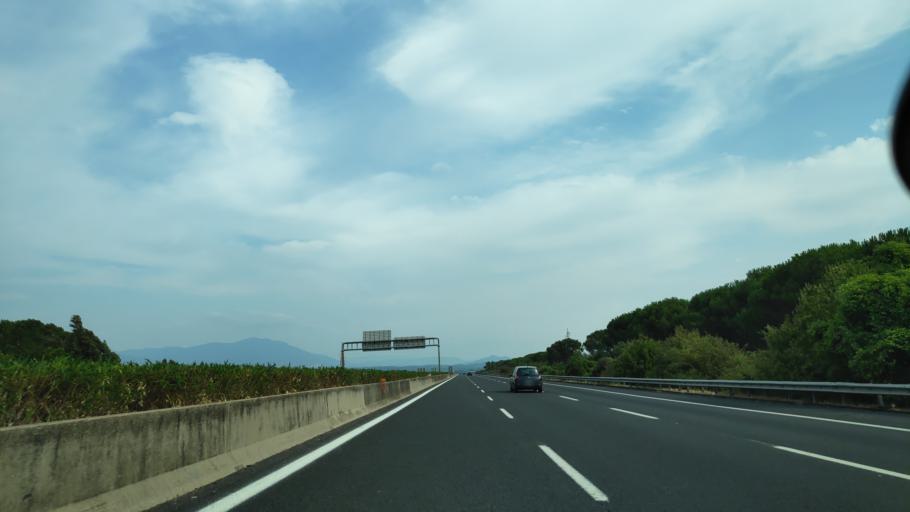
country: IT
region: Latium
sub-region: Citta metropolitana di Roma Capitale
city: Fiano Romano
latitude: 42.1656
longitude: 12.6158
